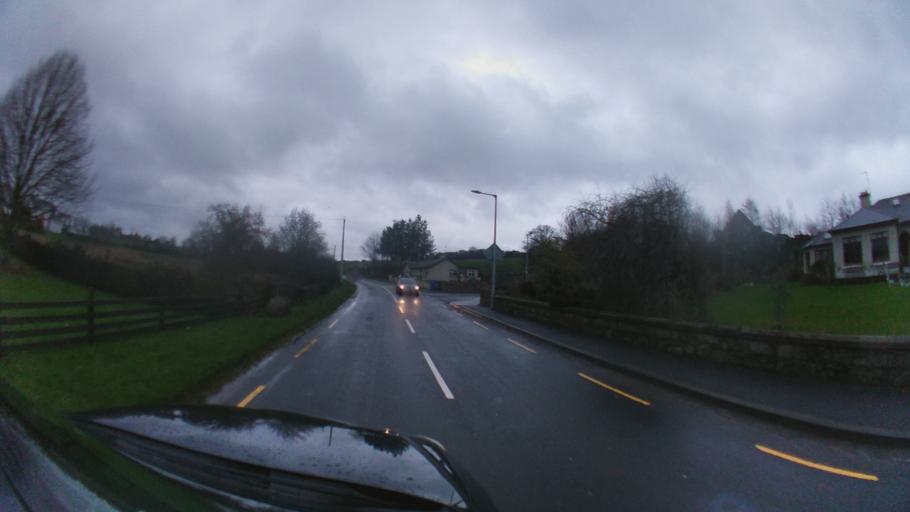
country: IE
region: Leinster
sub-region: Kilkenny
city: Graiguenamanagh
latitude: 52.5447
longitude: -6.9591
